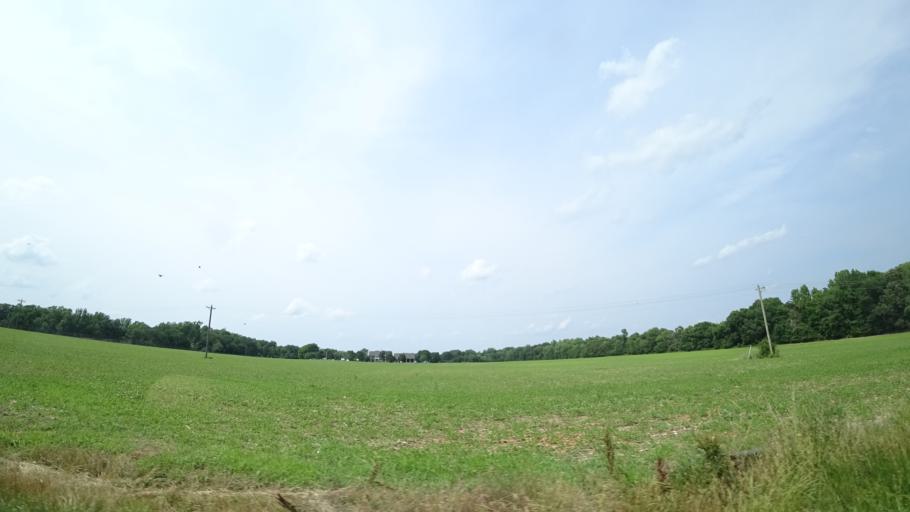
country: US
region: Virginia
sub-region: Spotsylvania County
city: Spotsylvania Courthouse
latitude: 38.1343
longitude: -77.5277
